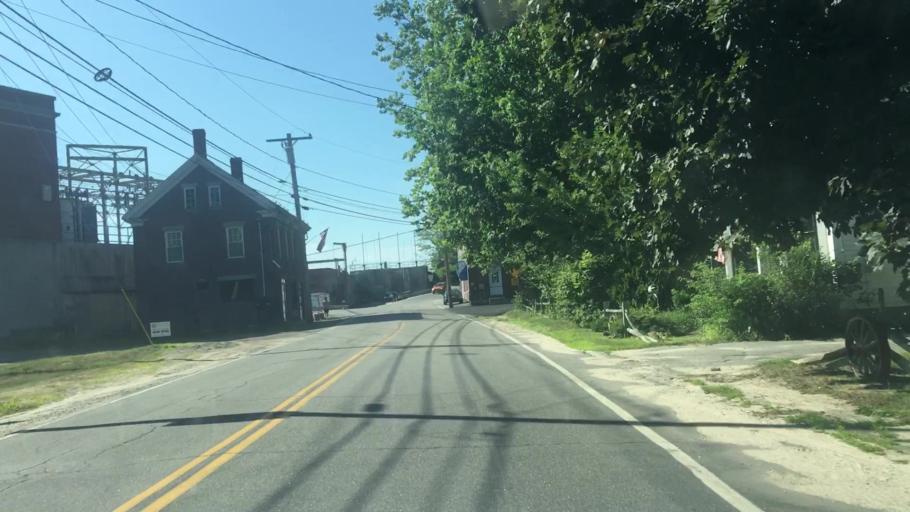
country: US
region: Maine
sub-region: York County
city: Hollis Center
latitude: 43.6660
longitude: -70.6010
